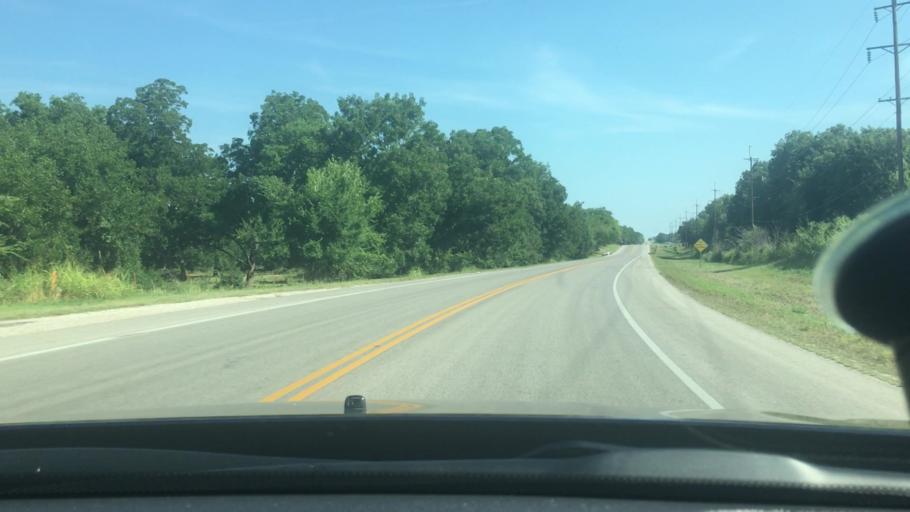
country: US
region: Oklahoma
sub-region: Garvin County
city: Pauls Valley
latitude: 34.6854
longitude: -97.2128
